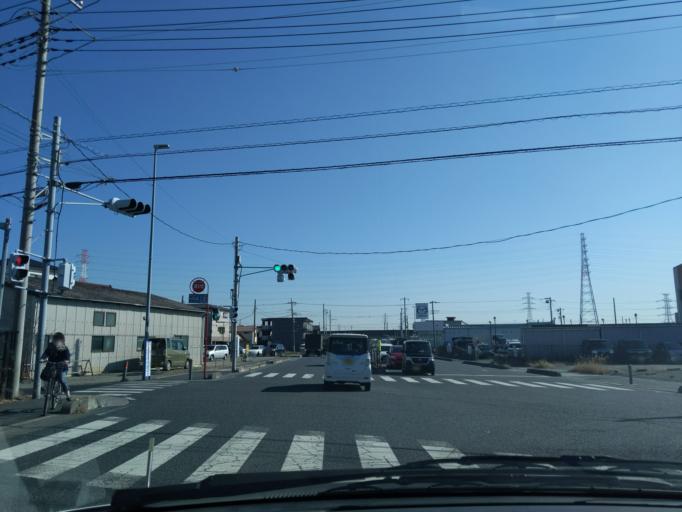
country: JP
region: Saitama
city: Yashio-shi
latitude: 35.8166
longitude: 139.8525
